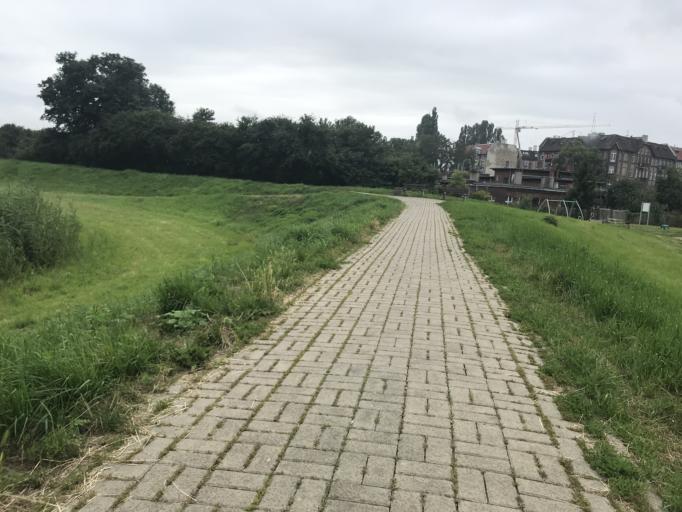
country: PL
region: Pomeranian Voivodeship
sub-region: Gdansk
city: Gdansk
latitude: 54.3426
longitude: 18.6673
